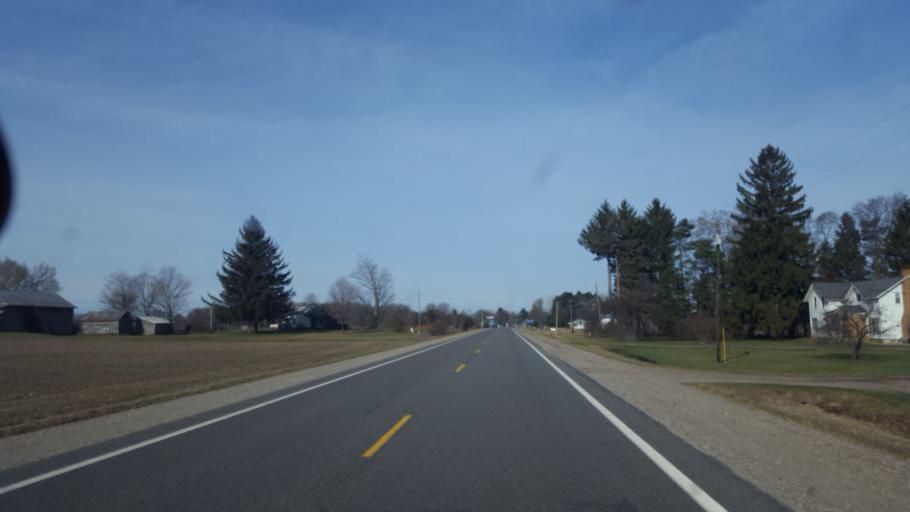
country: US
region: Michigan
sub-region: Montcalm County
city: Howard City
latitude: 43.4321
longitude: -85.3749
